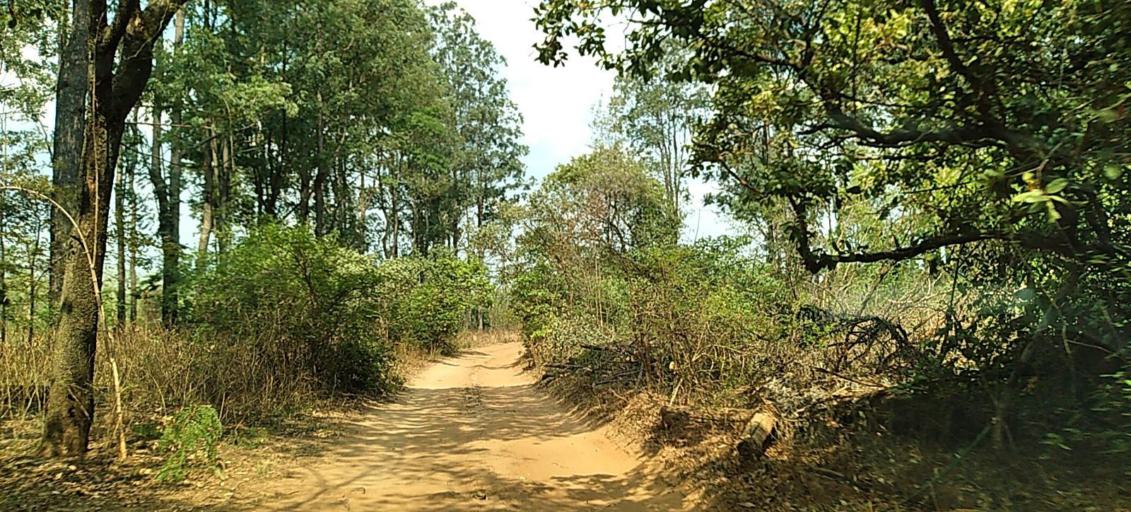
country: ZM
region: Copperbelt
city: Chingola
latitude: -12.7382
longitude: 27.7684
